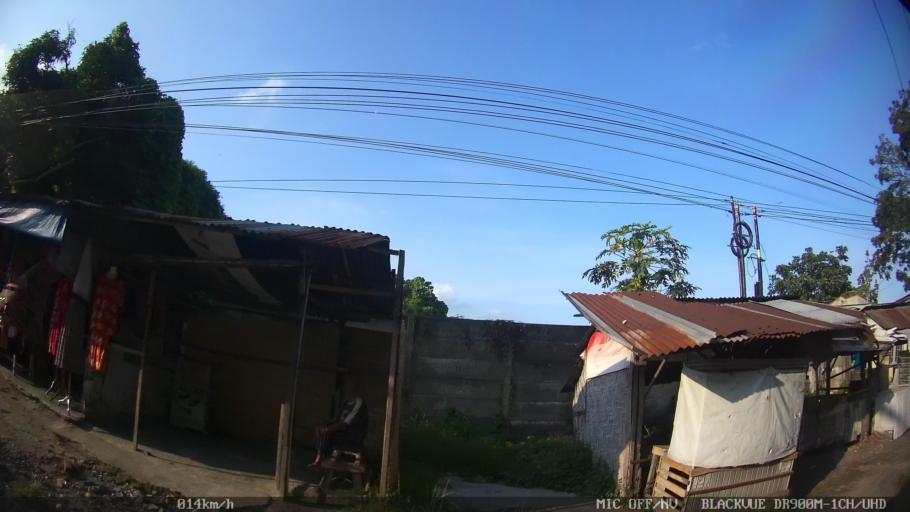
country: ID
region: North Sumatra
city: Medan
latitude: 3.6242
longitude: 98.6644
